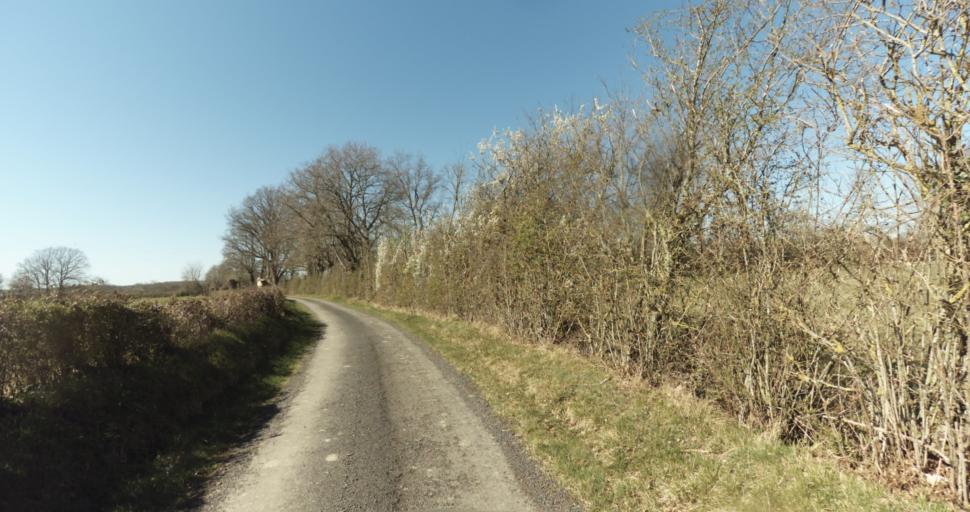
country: FR
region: Lower Normandy
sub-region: Departement du Calvados
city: Livarot
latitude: 48.9931
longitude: 0.1066
